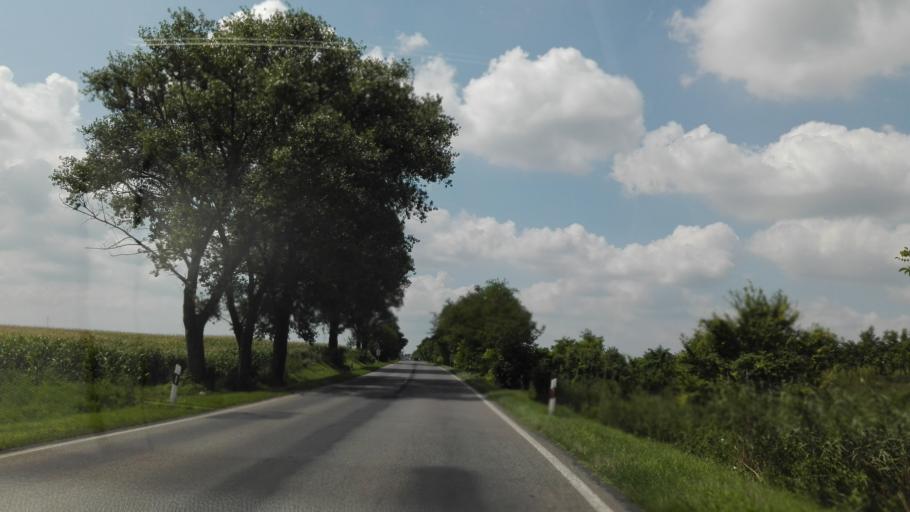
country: HU
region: Fejer
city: Eloszallas
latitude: 46.8292
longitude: 18.8506
